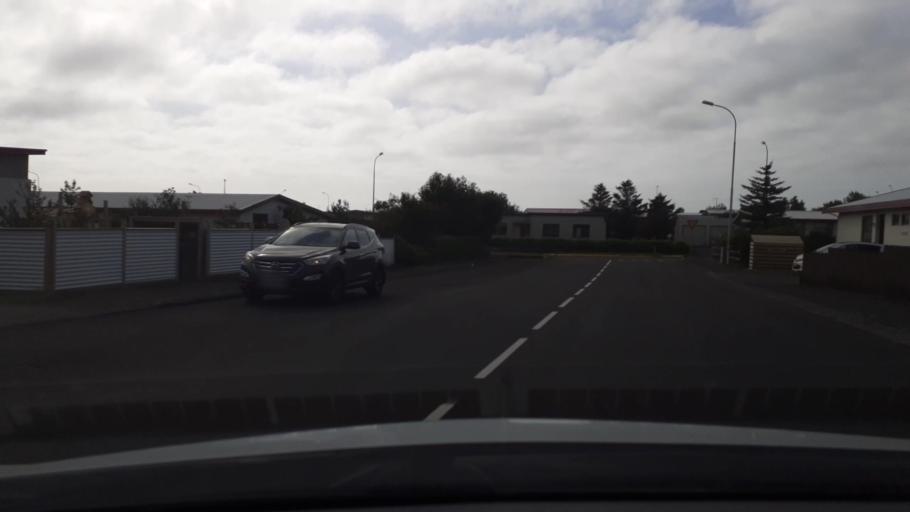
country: IS
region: South
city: THorlakshoefn
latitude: 63.8540
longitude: -21.3898
